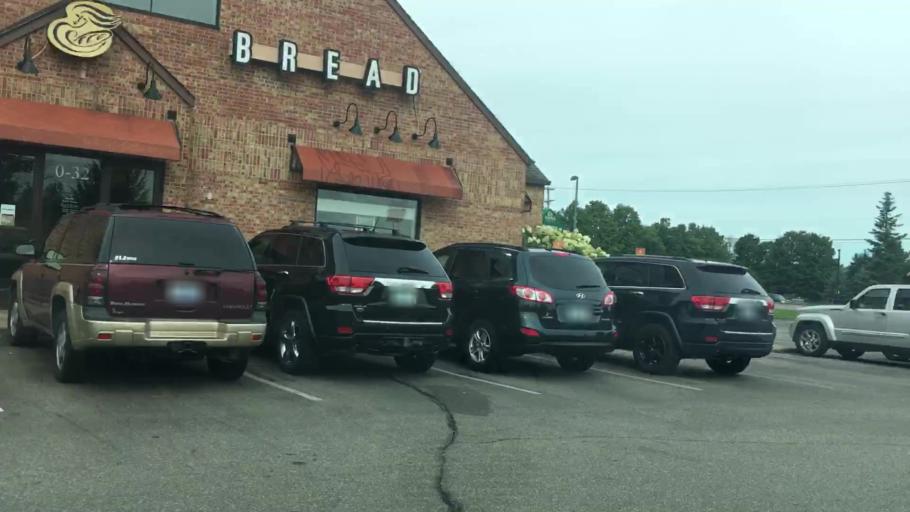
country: US
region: Michigan
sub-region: Ottawa County
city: Jenison
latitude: 42.8846
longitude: -85.7827
